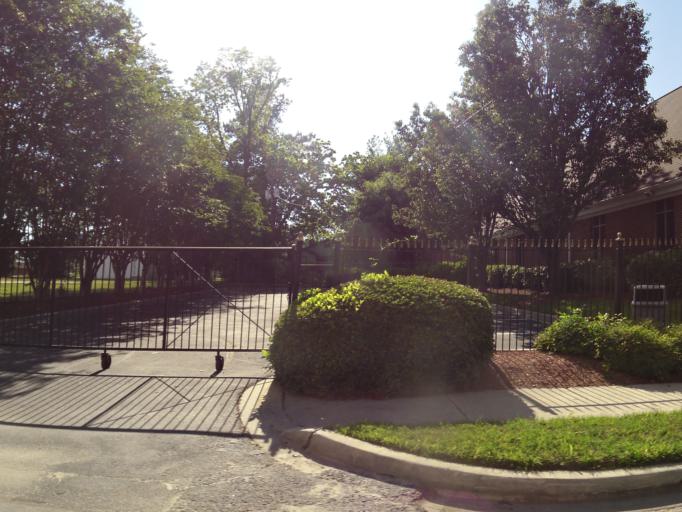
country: US
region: South Carolina
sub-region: Allendale County
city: Fairfax
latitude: 32.9528
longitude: -81.2360
